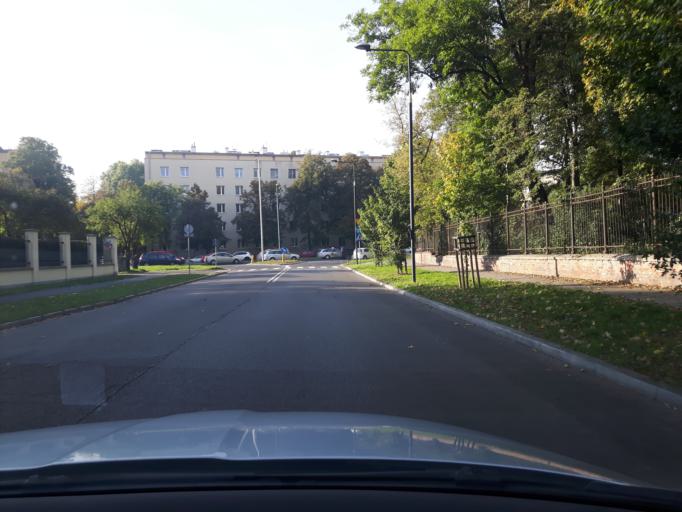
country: PL
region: Masovian Voivodeship
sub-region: Warszawa
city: Mokotow
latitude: 52.2076
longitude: 21.0352
